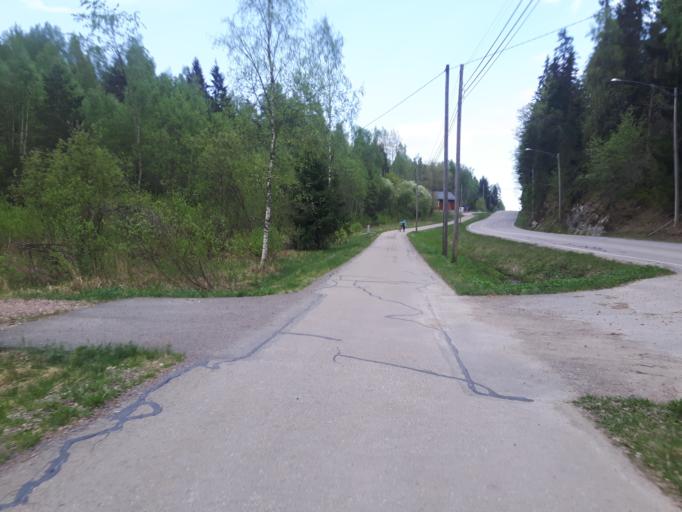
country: FI
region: Uusimaa
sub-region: Porvoo
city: Porvoo
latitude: 60.3991
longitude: 25.7293
